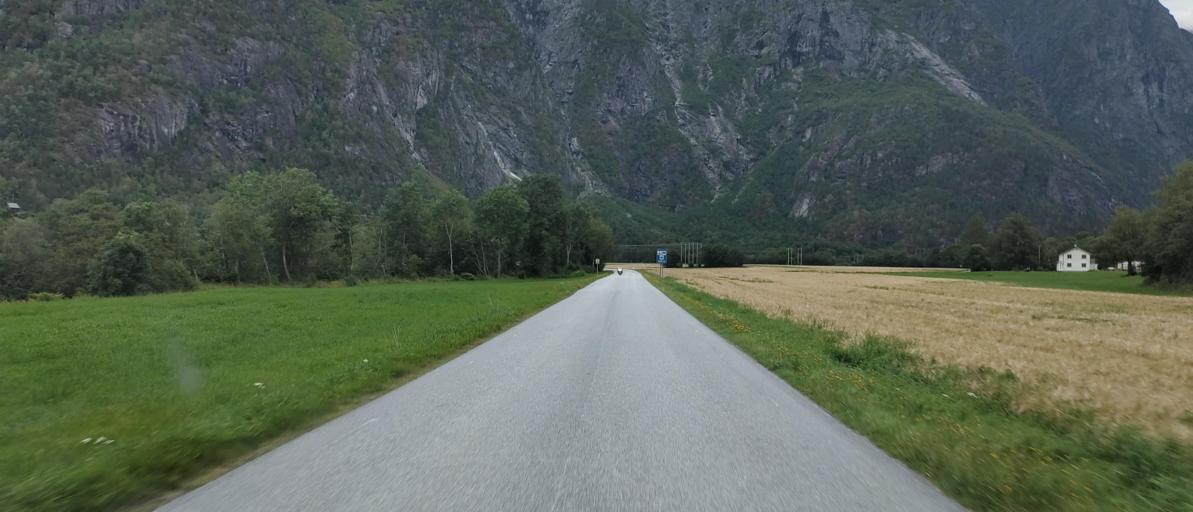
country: NO
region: More og Romsdal
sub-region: Rauma
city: Andalsnes
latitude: 62.5294
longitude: 7.7288
